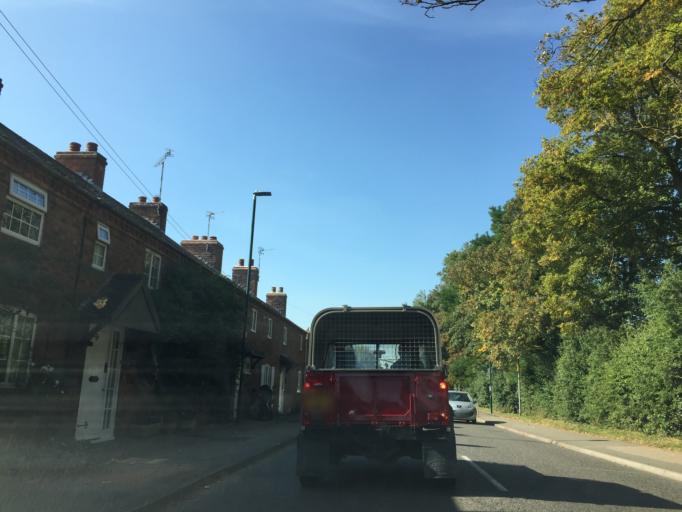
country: GB
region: England
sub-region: Leicestershire
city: Queniborough
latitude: 52.7049
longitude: -1.0460
